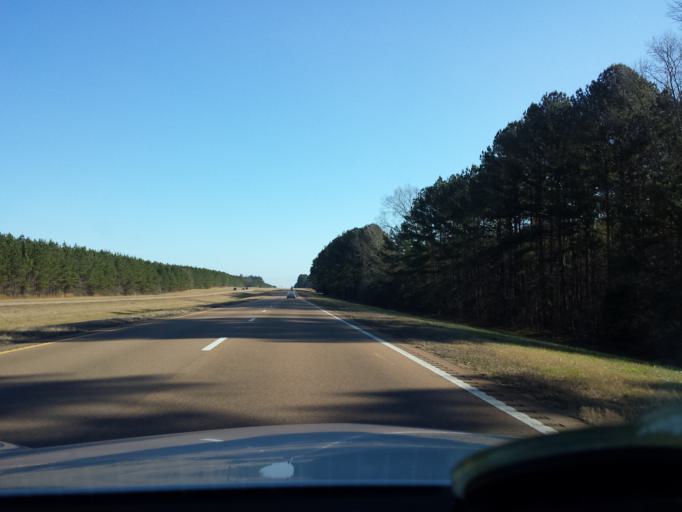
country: US
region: Mississippi
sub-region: Rankin County
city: Pelahatchie
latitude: 32.5440
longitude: -89.7988
